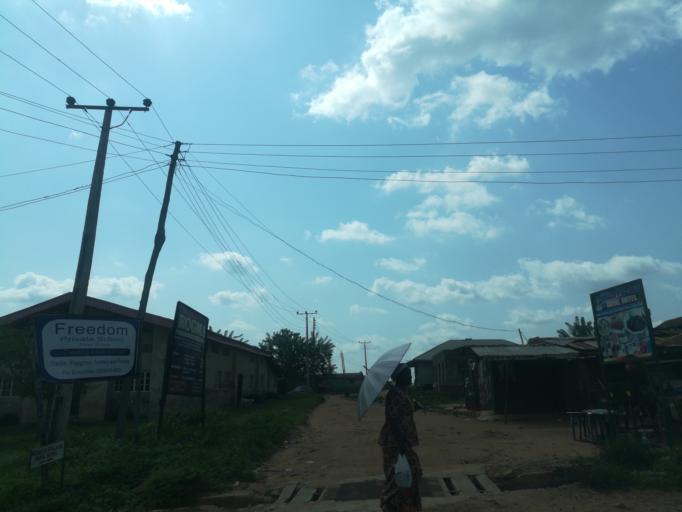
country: NG
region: Oyo
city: Moniya
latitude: 7.5369
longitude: 3.9116
